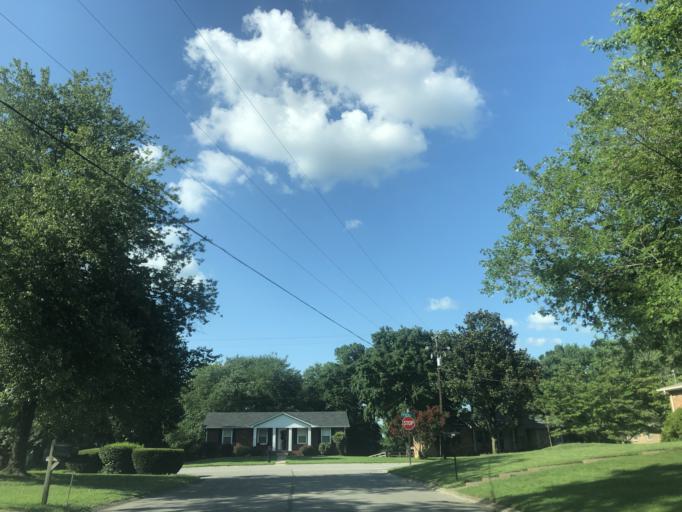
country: US
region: Tennessee
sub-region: Wilson County
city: Green Hill
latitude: 36.2119
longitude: -86.5946
